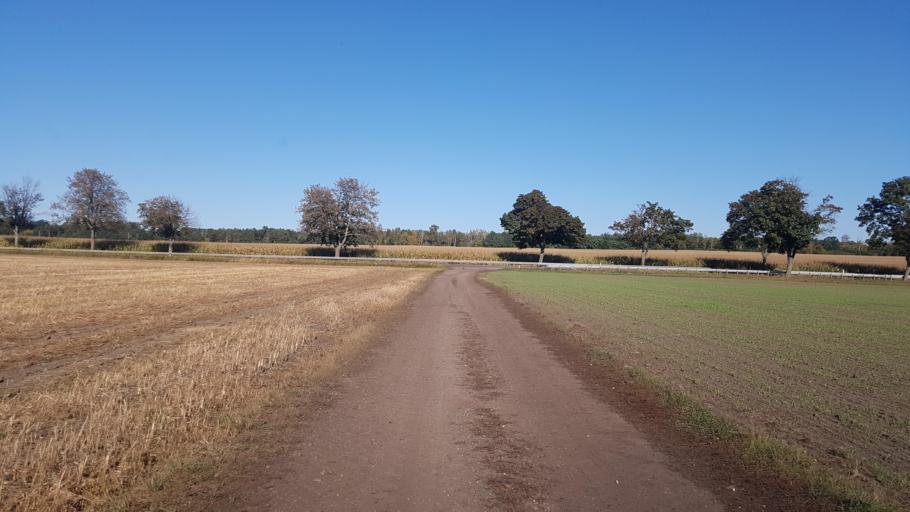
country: DE
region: Brandenburg
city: Plessa
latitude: 51.4673
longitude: 13.5882
